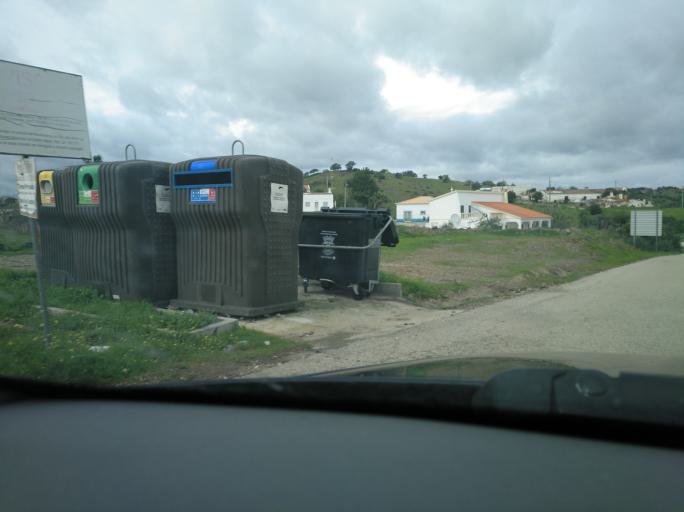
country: PT
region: Faro
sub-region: Castro Marim
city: Castro Marim
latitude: 37.2212
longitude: -7.4892
